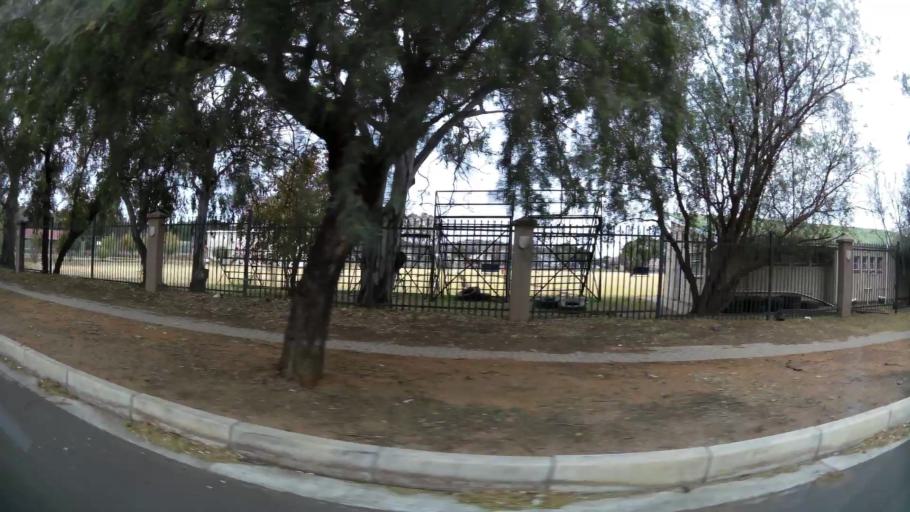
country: ZA
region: Orange Free State
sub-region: Mangaung Metropolitan Municipality
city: Bloemfontein
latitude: -29.1050
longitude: 26.2036
